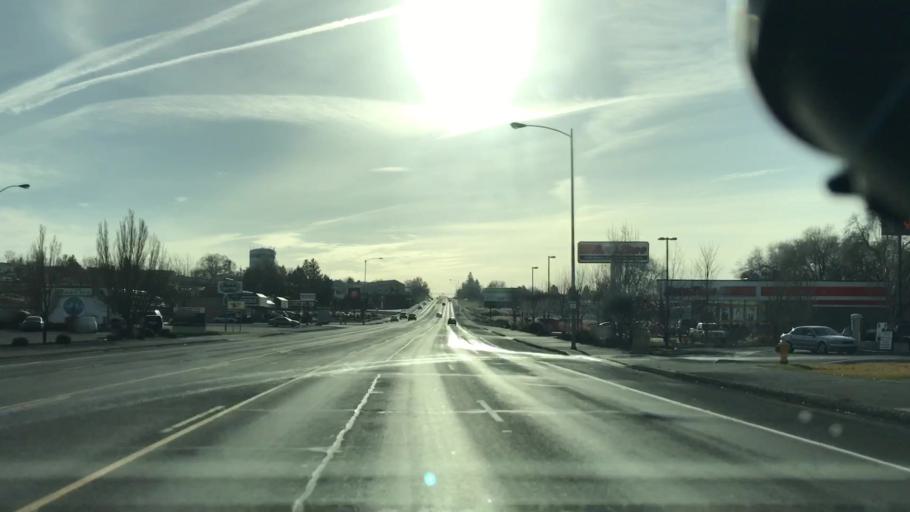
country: US
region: Washington
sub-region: Grant County
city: Moses Lake
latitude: 47.1297
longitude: -119.2697
